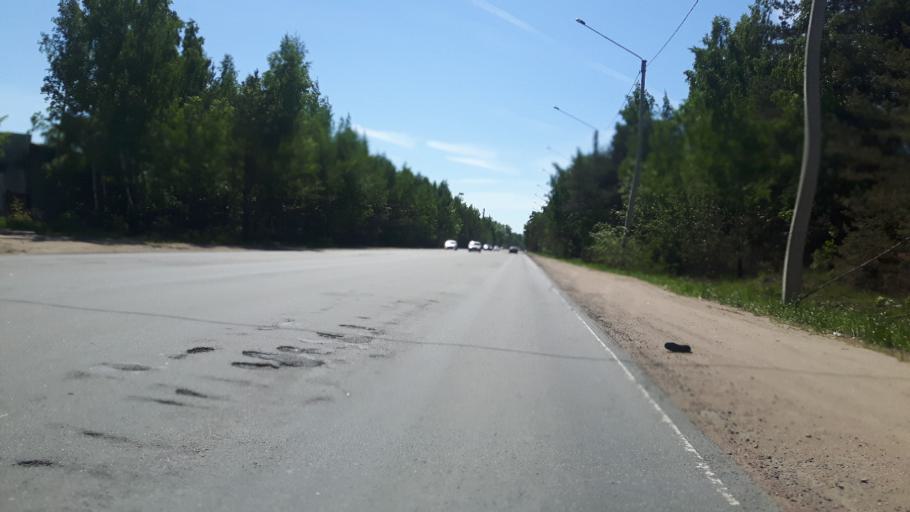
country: RU
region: Leningrad
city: Sosnovyy Bor
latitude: 59.8720
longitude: 29.0833
